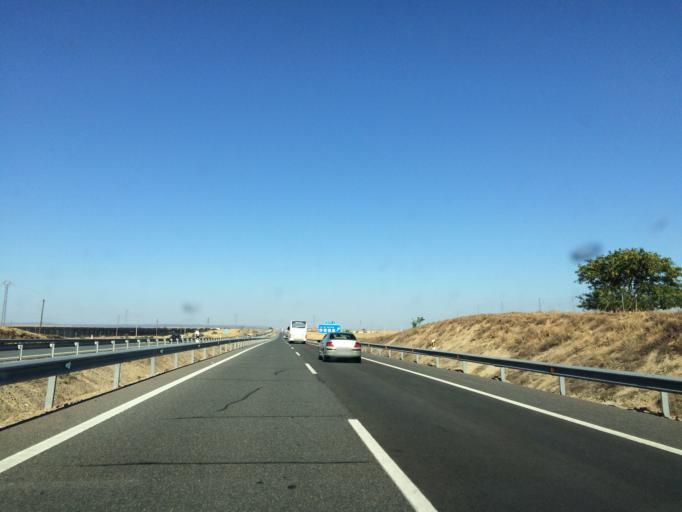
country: ES
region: Castille-La Mancha
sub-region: Province of Toledo
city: Caleruela
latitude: 39.8952
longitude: -5.3129
